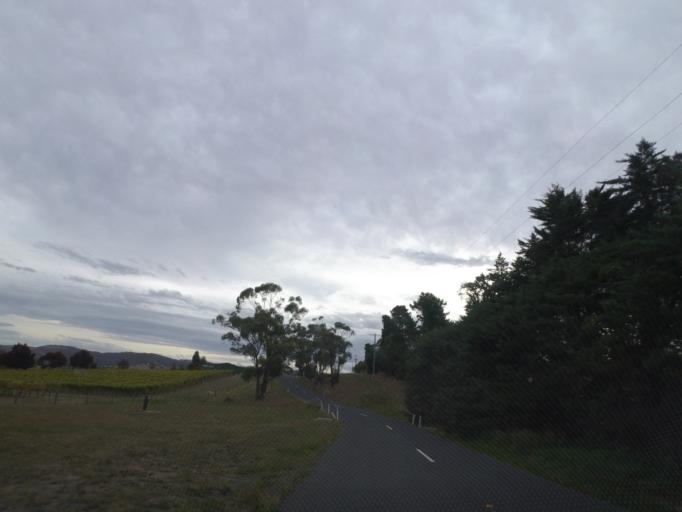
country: AU
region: Victoria
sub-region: Yarra Ranges
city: Yarra Glen
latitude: -37.6324
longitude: 145.3986
